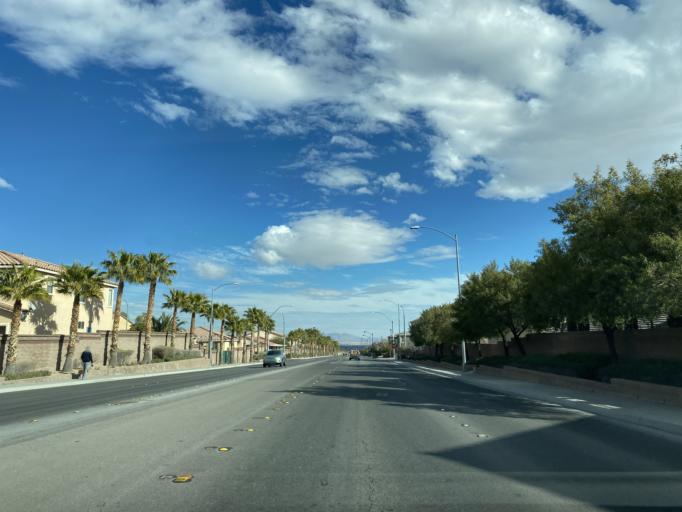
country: US
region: Nevada
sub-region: Clark County
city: Summerlin South
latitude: 36.2846
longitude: -115.3028
